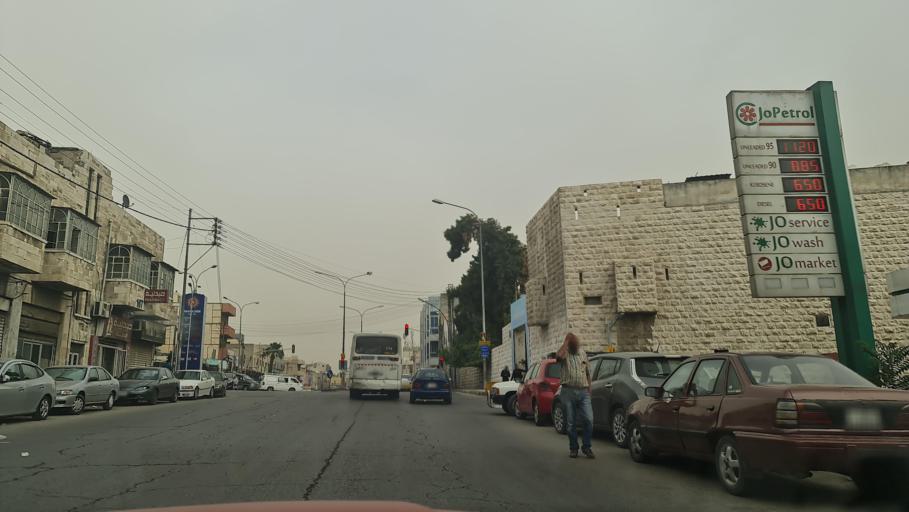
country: JO
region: Amman
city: Al Quwaysimah
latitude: 31.9332
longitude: 35.9334
